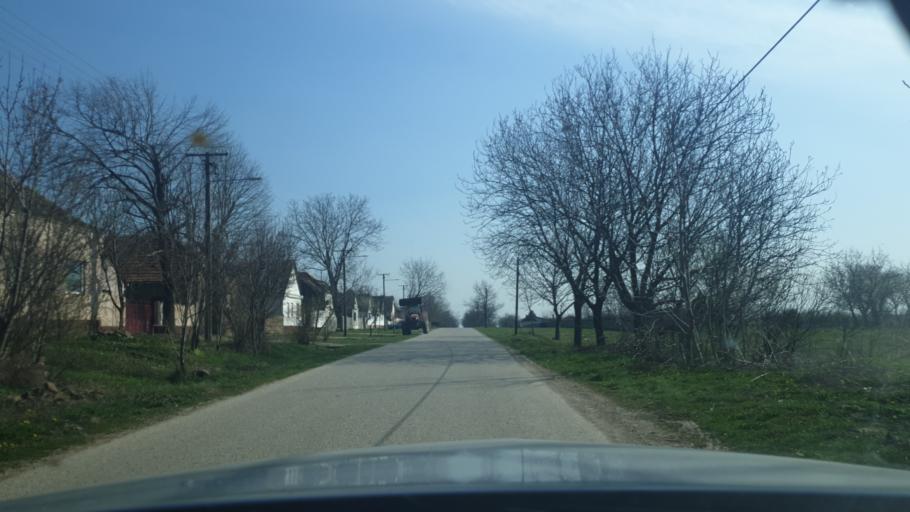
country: RS
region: Autonomna Pokrajina Vojvodina
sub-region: Sremski Okrug
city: Irig
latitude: 45.0656
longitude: 19.9232
